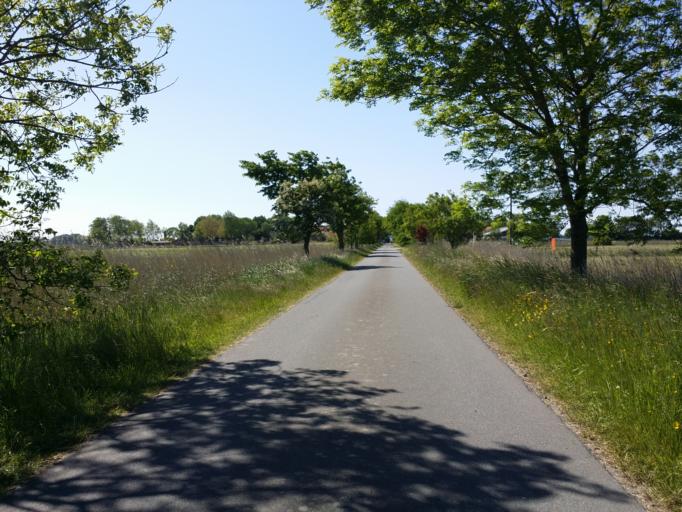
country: DE
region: Lower Saxony
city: Esens
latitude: 53.6744
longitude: 7.6400
